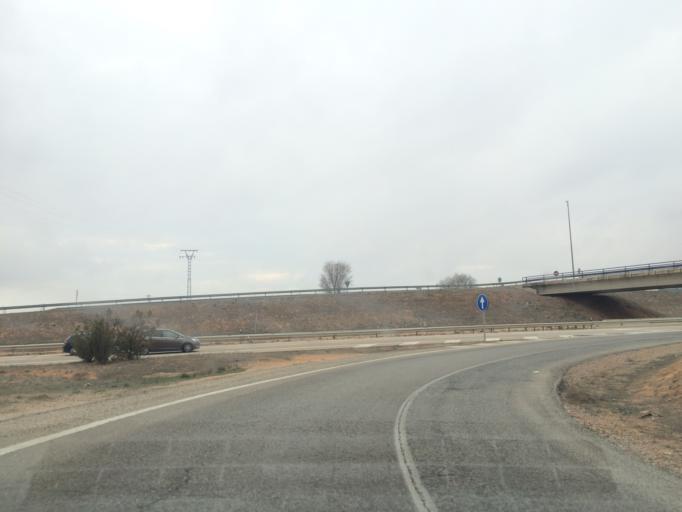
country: ES
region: Castille-La Mancha
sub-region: Province of Toledo
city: Madridejos
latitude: 39.4783
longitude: -3.5222
